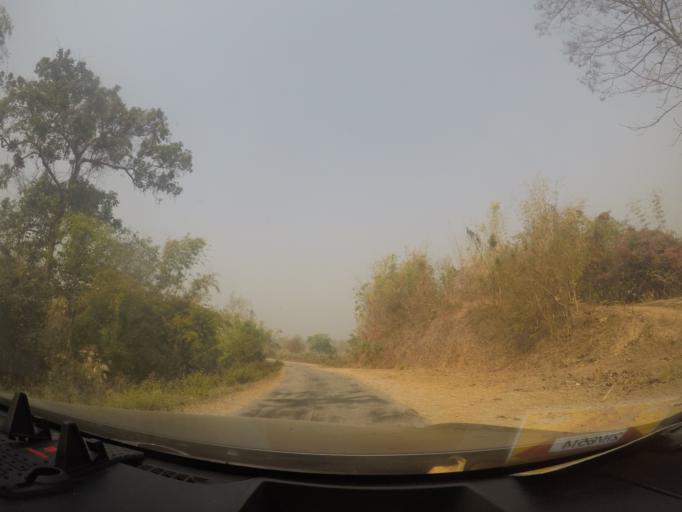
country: MM
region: Magway
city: Taungdwingyi
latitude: 19.9318
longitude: 95.8217
